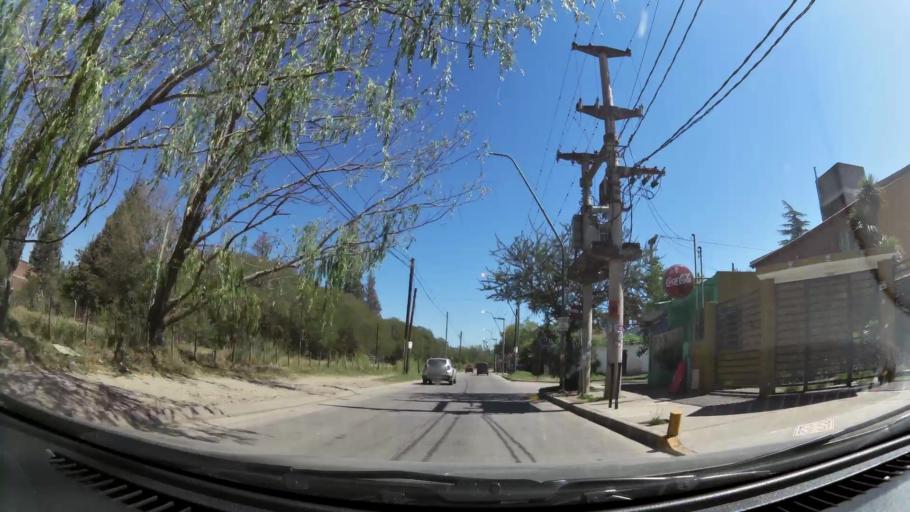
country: AR
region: Cordoba
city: Saldan
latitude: -31.3373
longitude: -64.2844
